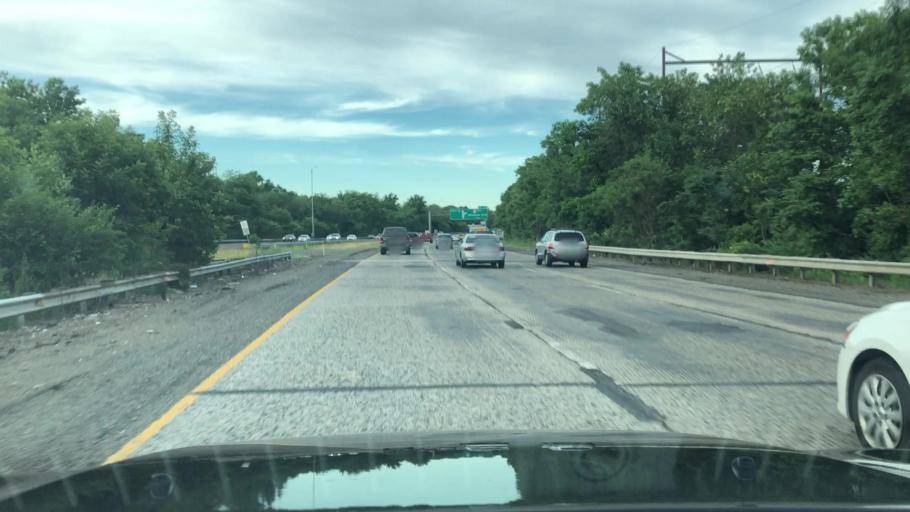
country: US
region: New Jersey
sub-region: Burlington County
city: Delanco
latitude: 40.0567
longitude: -74.9830
